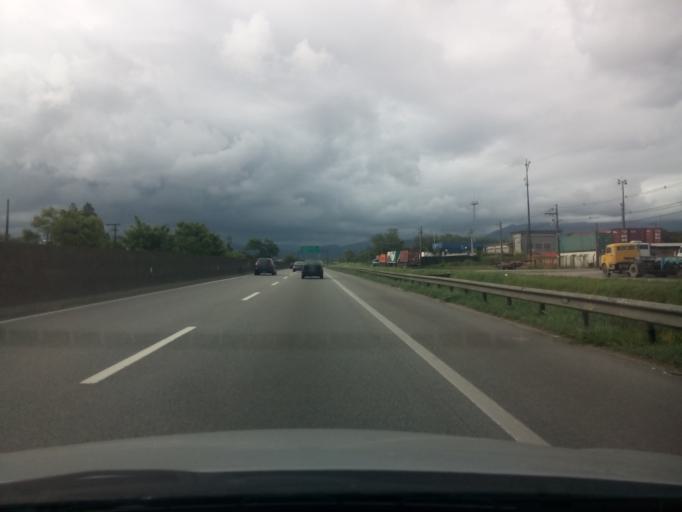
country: BR
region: Sao Paulo
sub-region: Guaruja
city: Guaruja
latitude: -23.9502
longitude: -46.2772
